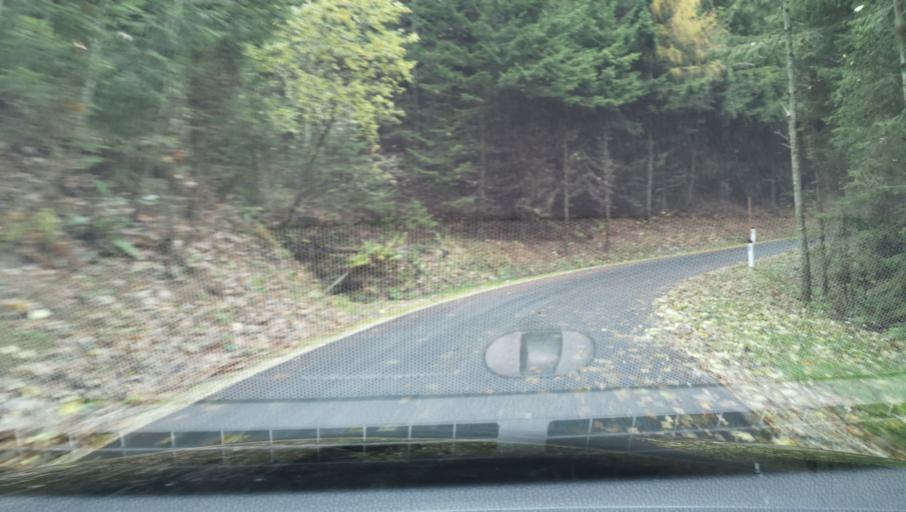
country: AT
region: Styria
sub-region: Politischer Bezirk Weiz
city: Gasen
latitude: 47.3562
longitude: 15.5898
